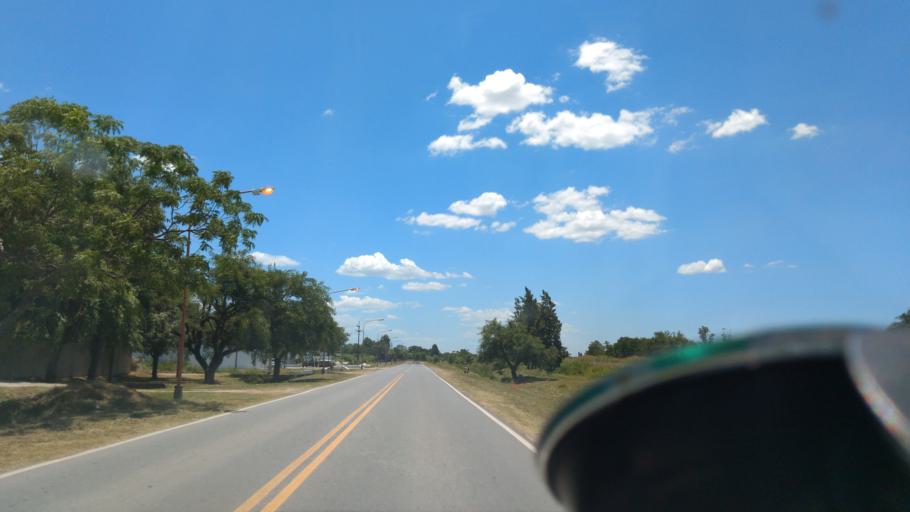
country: AR
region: Santa Fe
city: Laguna Paiva
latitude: -31.3193
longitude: -60.6587
